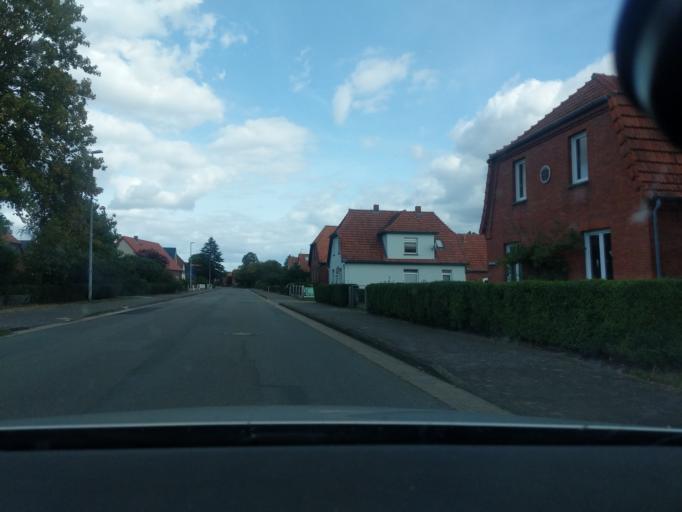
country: DE
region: Lower Saxony
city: Bucken
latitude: 52.7771
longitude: 9.1194
